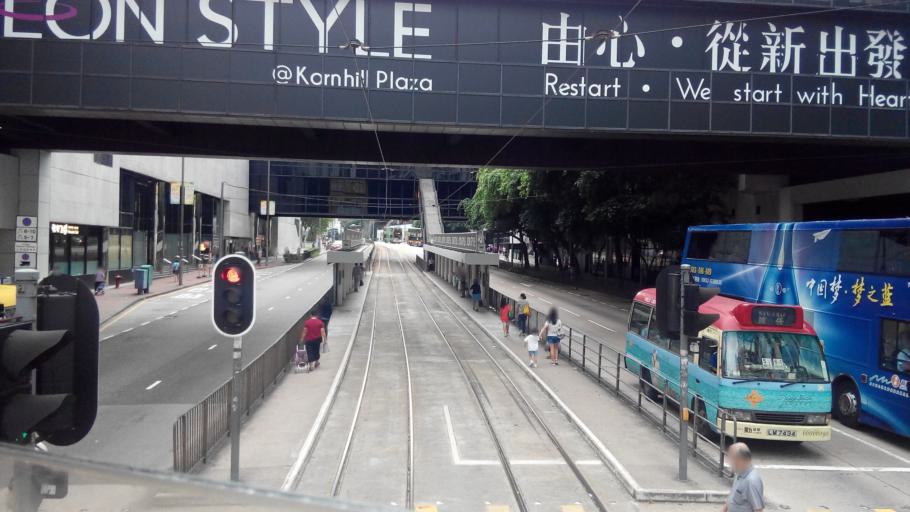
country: HK
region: Wanchai
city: Wan Chai
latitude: 22.2846
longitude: 114.2155
